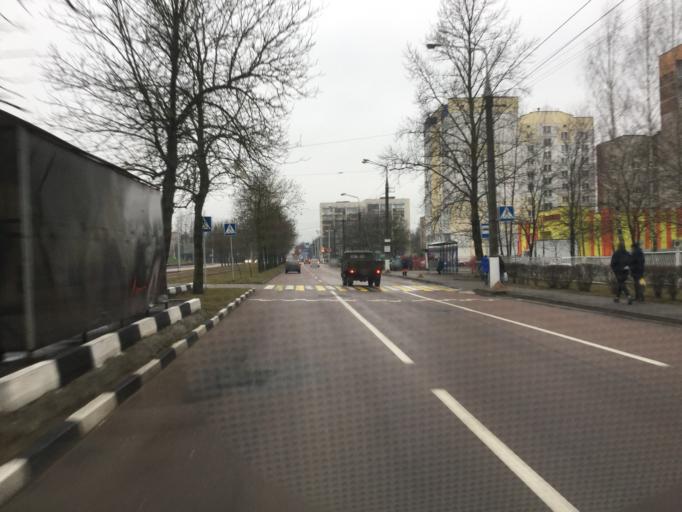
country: BY
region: Vitebsk
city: Vitebsk
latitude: 55.1962
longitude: 30.2529
